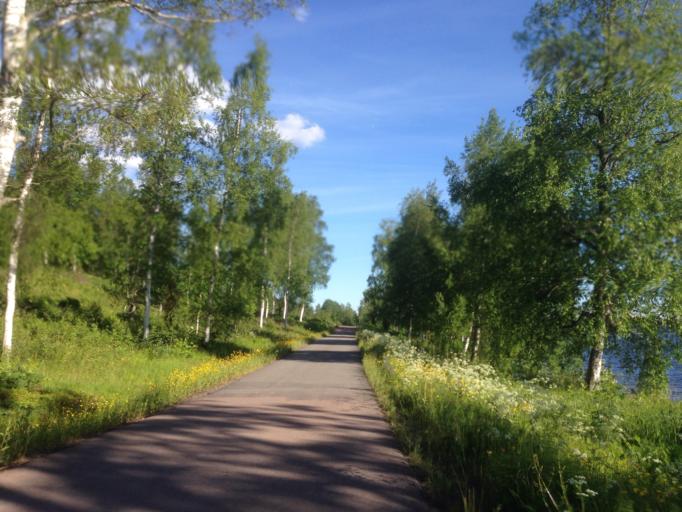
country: SE
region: Dalarna
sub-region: Ludvika Kommun
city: Ludvika
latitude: 60.1145
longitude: 15.2038
